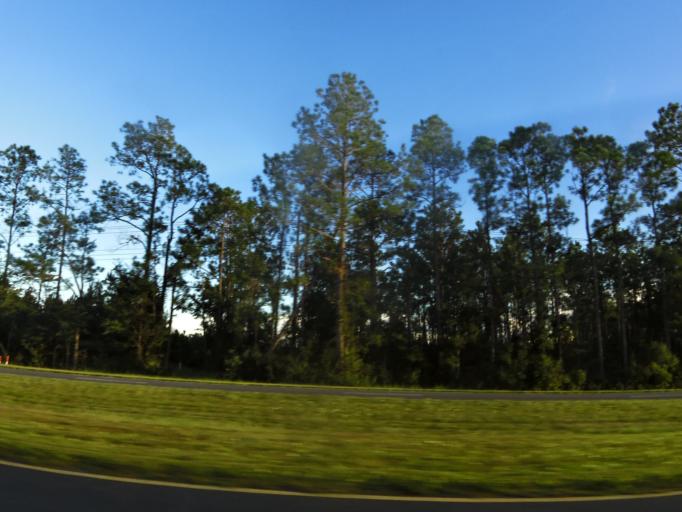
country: US
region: Georgia
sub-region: Camden County
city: Kings Bay Base
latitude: 30.7909
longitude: -81.5892
